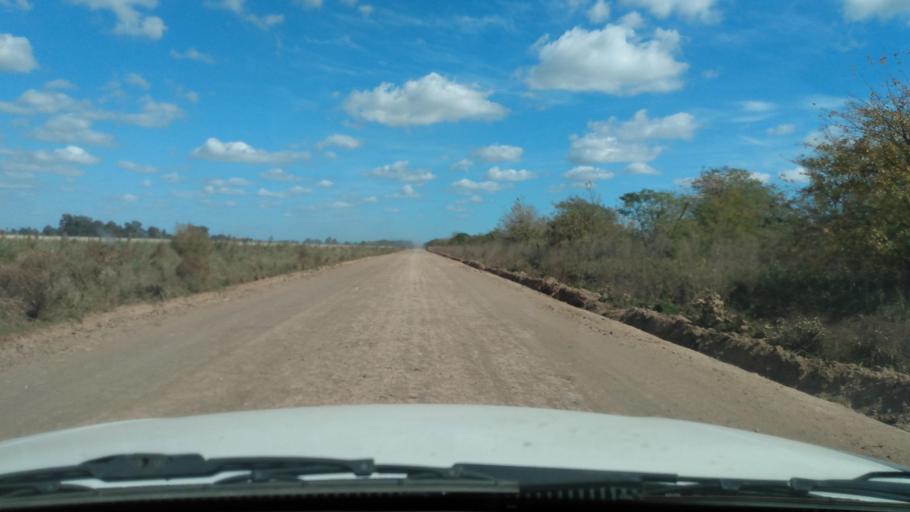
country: AR
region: Buenos Aires
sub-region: Partido de Navarro
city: Navarro
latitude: -35.0258
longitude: -59.4407
